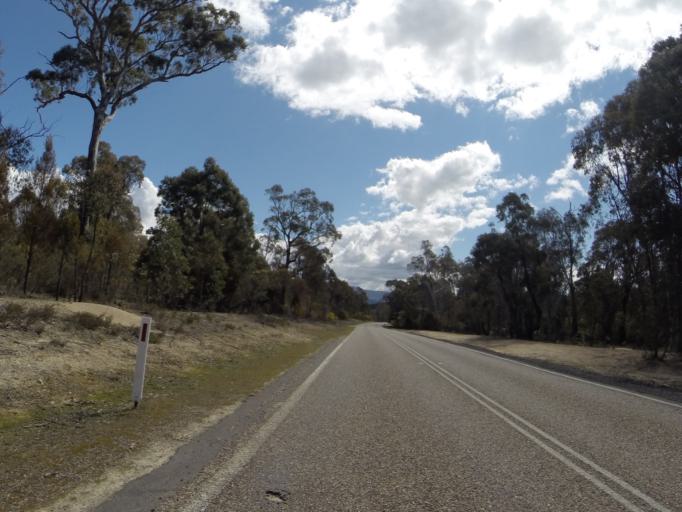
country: AU
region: Australian Capital Territory
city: Macquarie
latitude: -35.3480
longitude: 148.9326
